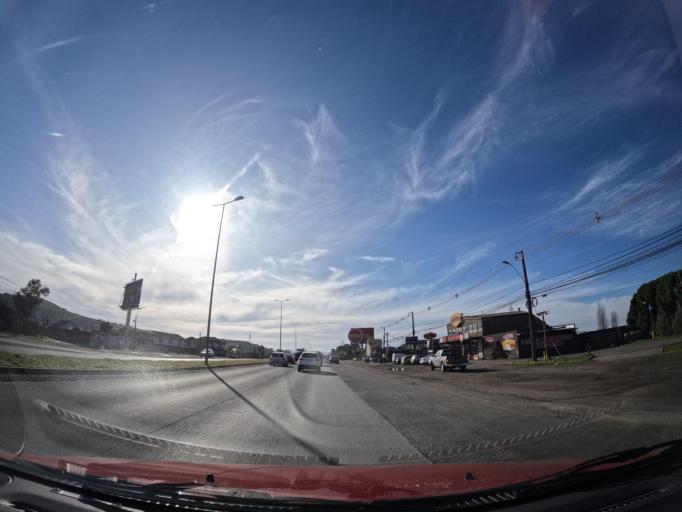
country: CL
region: Biobio
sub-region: Provincia de Concepcion
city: Talcahuano
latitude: -36.7721
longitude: -73.0820
